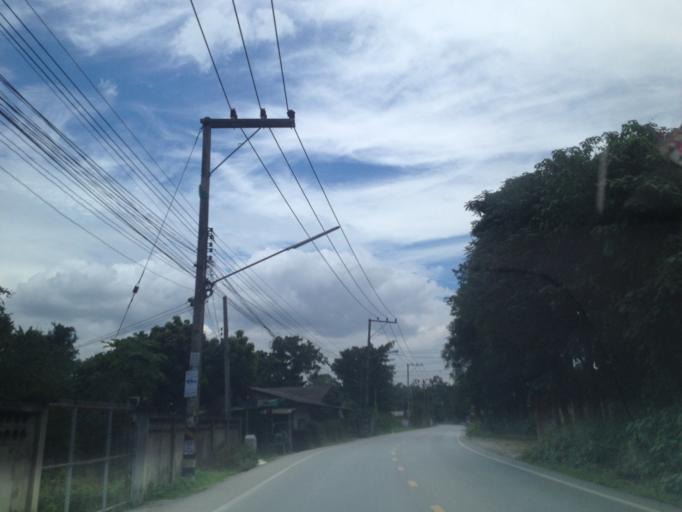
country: TH
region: Chiang Mai
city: Saraphi
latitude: 18.7238
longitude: 98.9860
